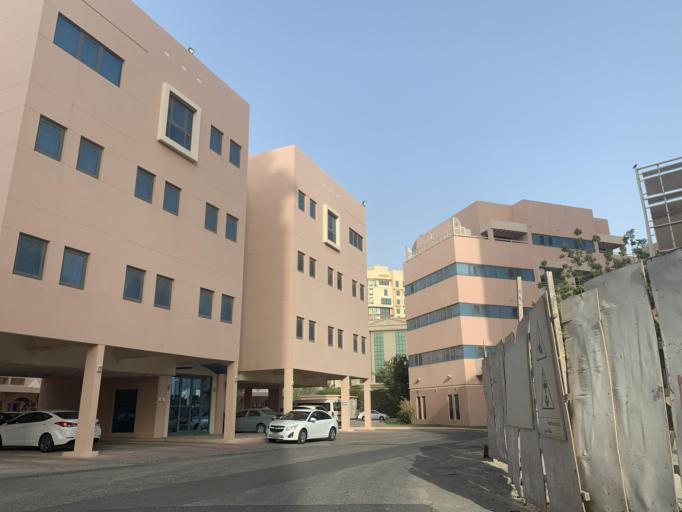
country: BH
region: Manama
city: Jidd Hafs
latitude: 26.2419
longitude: 50.5366
